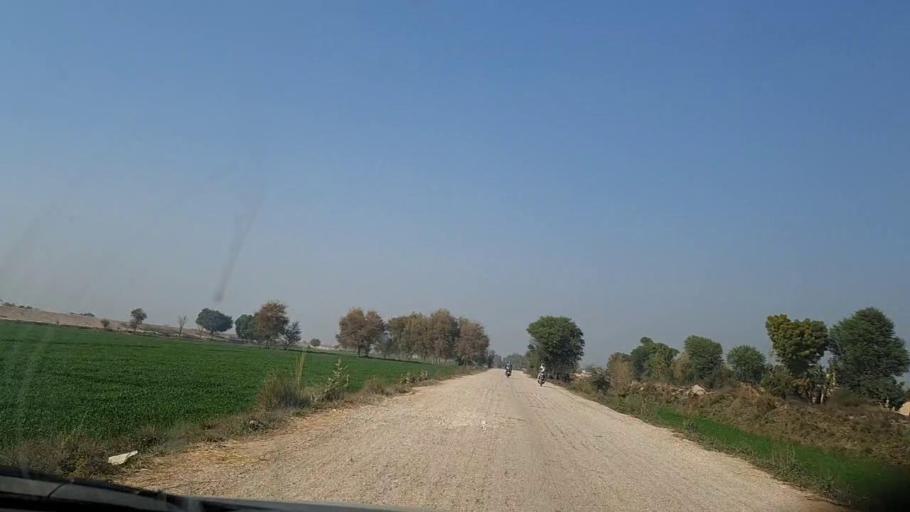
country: PK
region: Sindh
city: Moro
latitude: 26.7345
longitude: 67.9199
